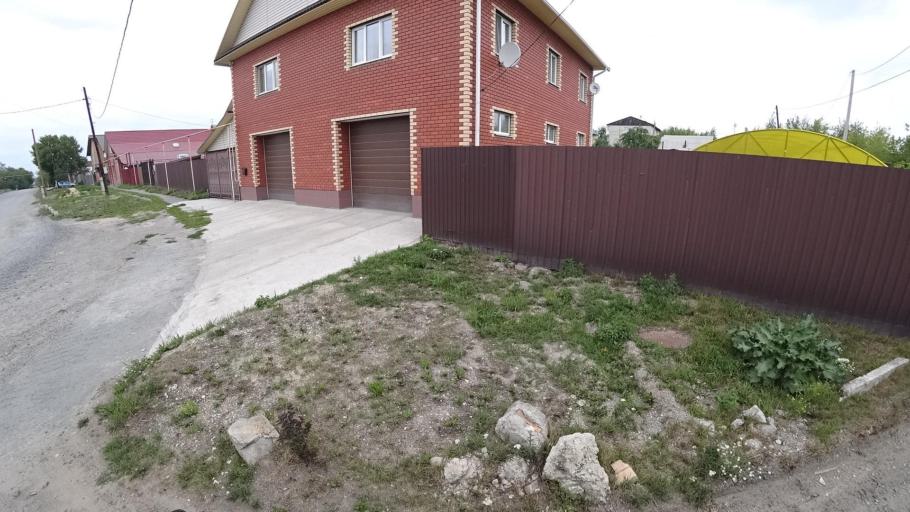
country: RU
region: Sverdlovsk
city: Kamyshlov
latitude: 56.8353
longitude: 62.7195
